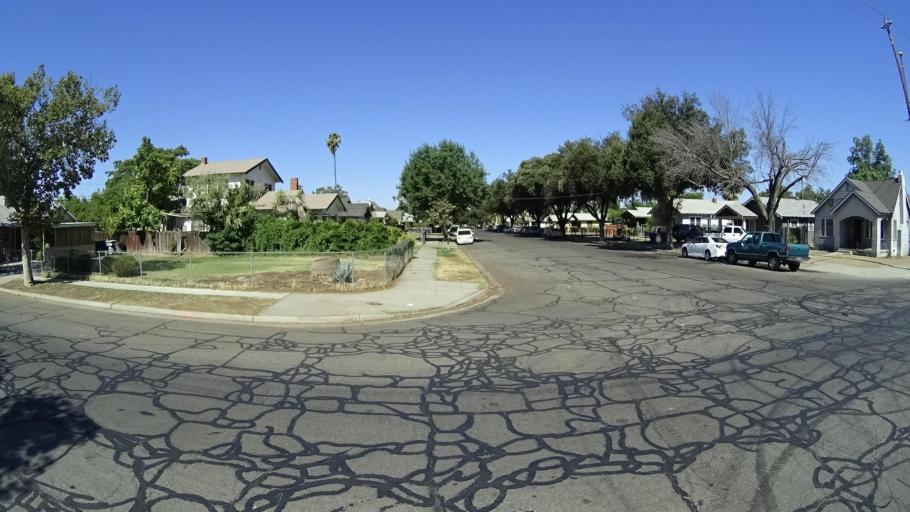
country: US
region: California
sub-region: Fresno County
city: Fresno
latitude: 36.7317
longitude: -119.7658
